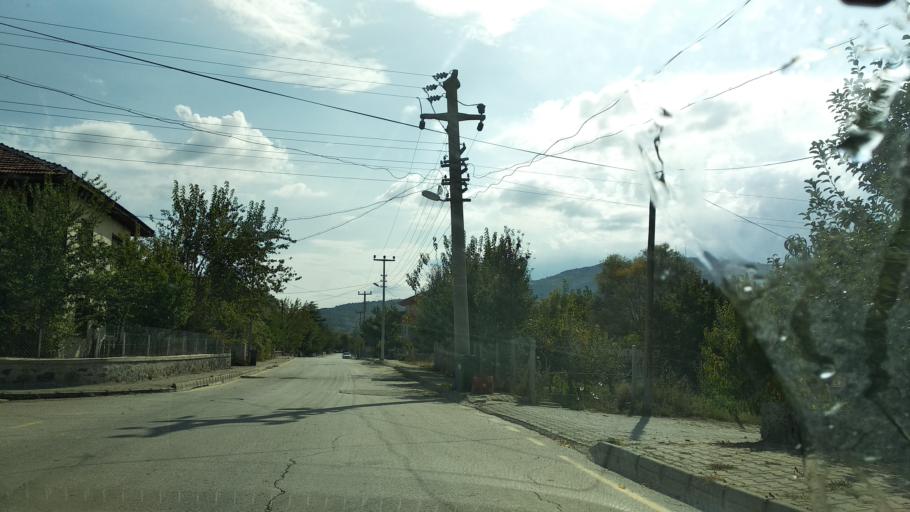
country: TR
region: Bolu
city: Seben
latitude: 40.4122
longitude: 31.5684
